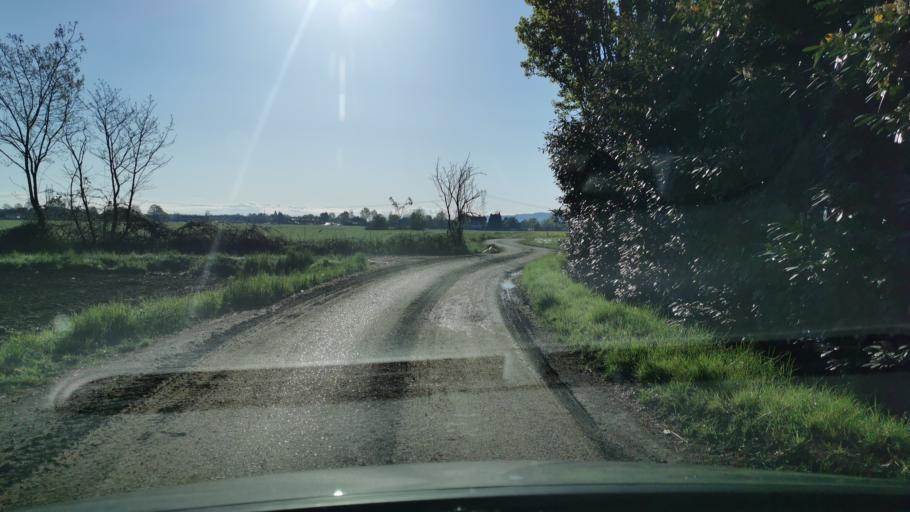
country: IT
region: Piedmont
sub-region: Provincia di Torino
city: Lombardore
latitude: 45.2170
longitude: 7.7097
